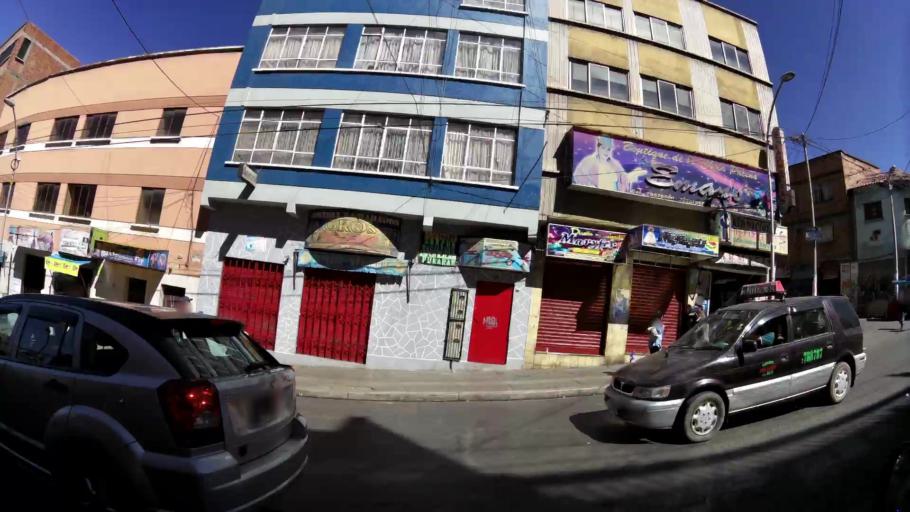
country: BO
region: La Paz
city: La Paz
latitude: -16.4957
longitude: -68.1480
